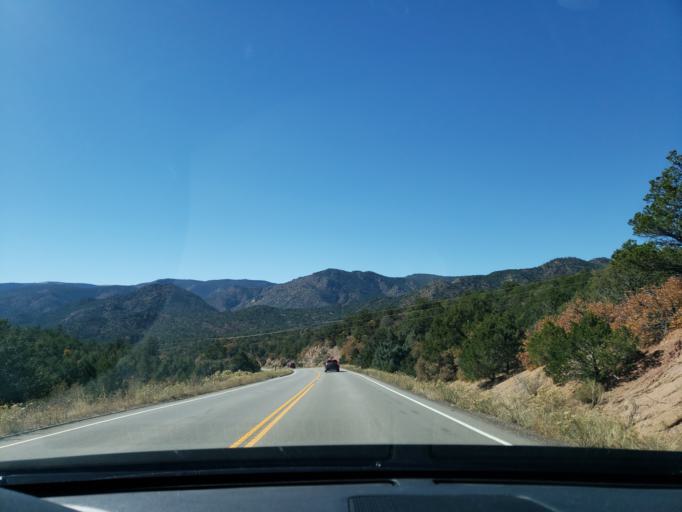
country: US
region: Colorado
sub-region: Fremont County
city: Canon City
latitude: 38.5791
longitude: -105.4197
